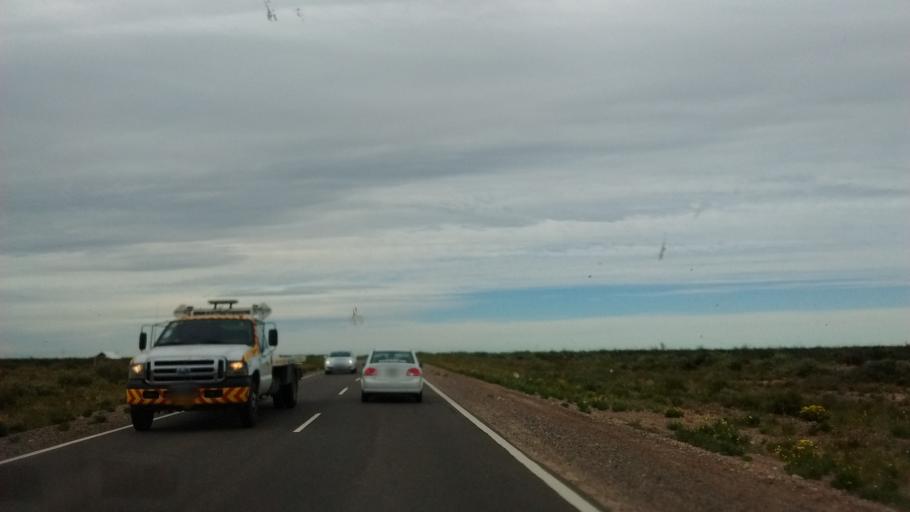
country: AR
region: Rio Negro
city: Contraalmirante Cordero
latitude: -38.3425
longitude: -68.0119
